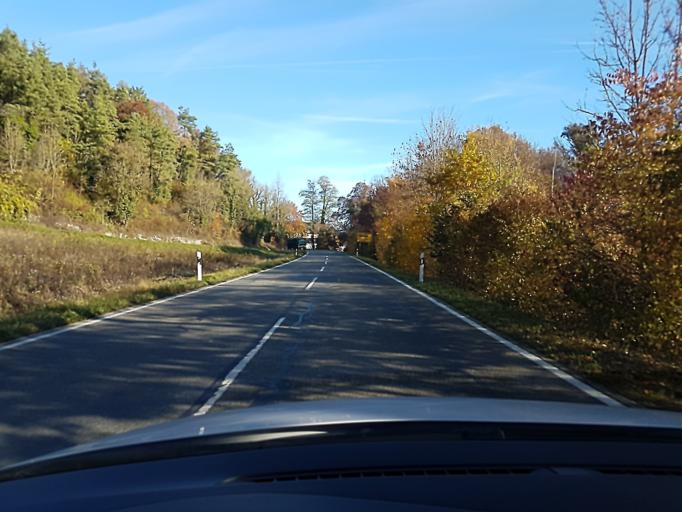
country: DE
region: Baden-Wuerttemberg
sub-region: Karlsruhe Region
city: Billigheim
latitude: 49.3451
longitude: 9.2529
